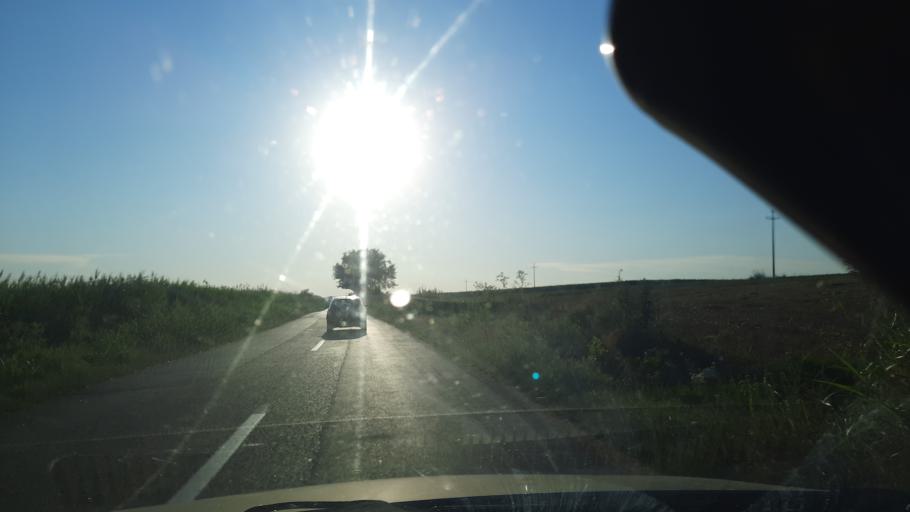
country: RS
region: Central Serbia
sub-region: Branicevski Okrug
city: Malo Crnice
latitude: 44.5786
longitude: 21.3306
